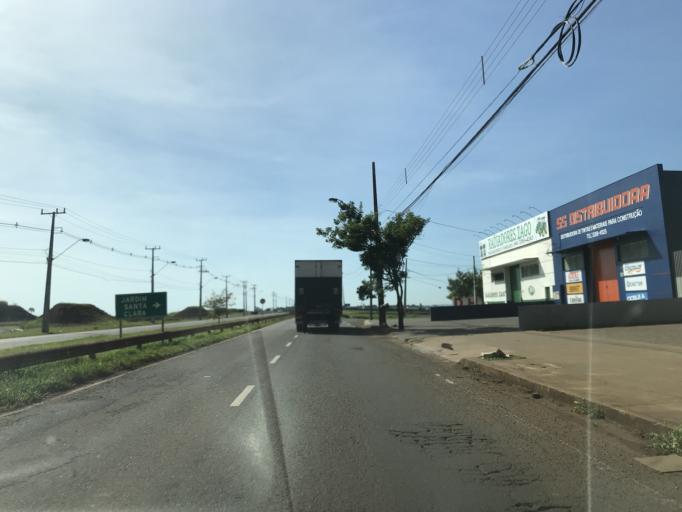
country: BR
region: Parana
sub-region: Maringa
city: Maringa
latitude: -23.3821
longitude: -51.9139
